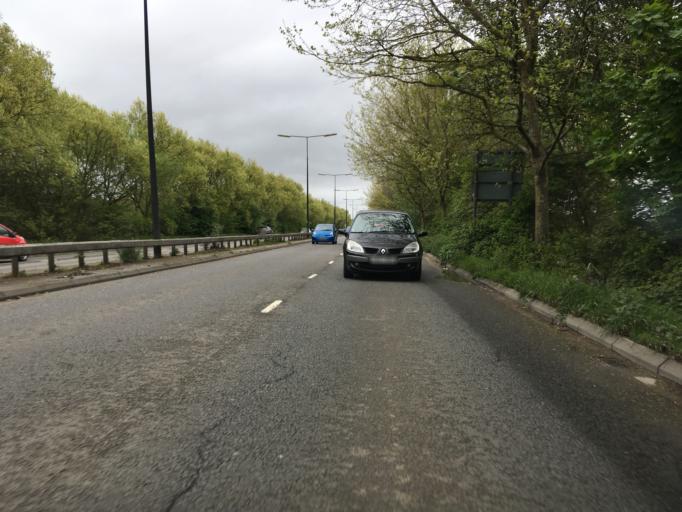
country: GB
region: England
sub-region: North Somerset
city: Kewstoke
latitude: 51.3432
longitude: -2.9494
